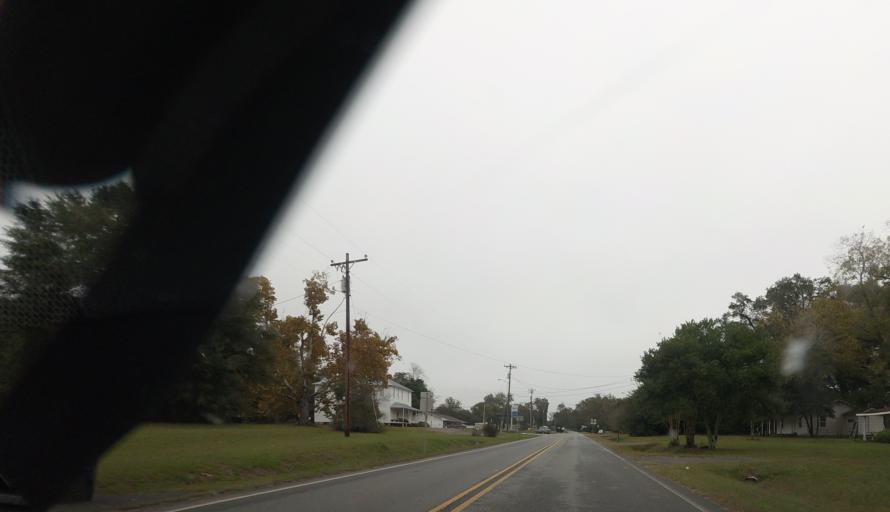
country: US
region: Georgia
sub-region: Marion County
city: Buena Vista
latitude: 32.3802
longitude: -84.4417
